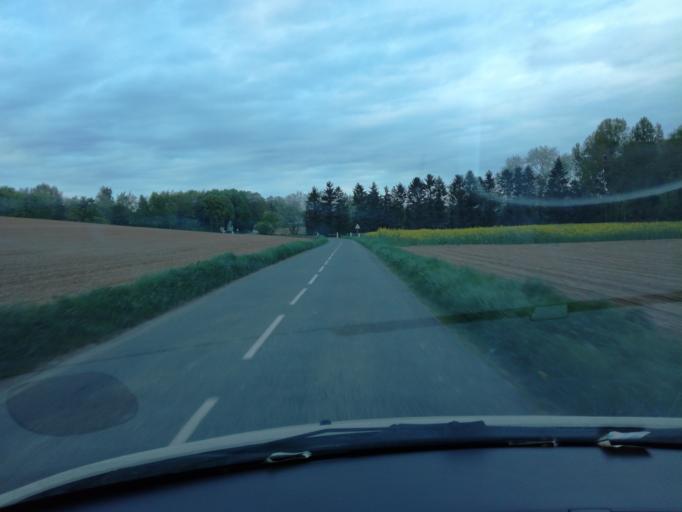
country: FR
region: Picardie
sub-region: Departement de la Somme
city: Poix-de-Picardie
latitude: 49.8160
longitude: 2.0164
